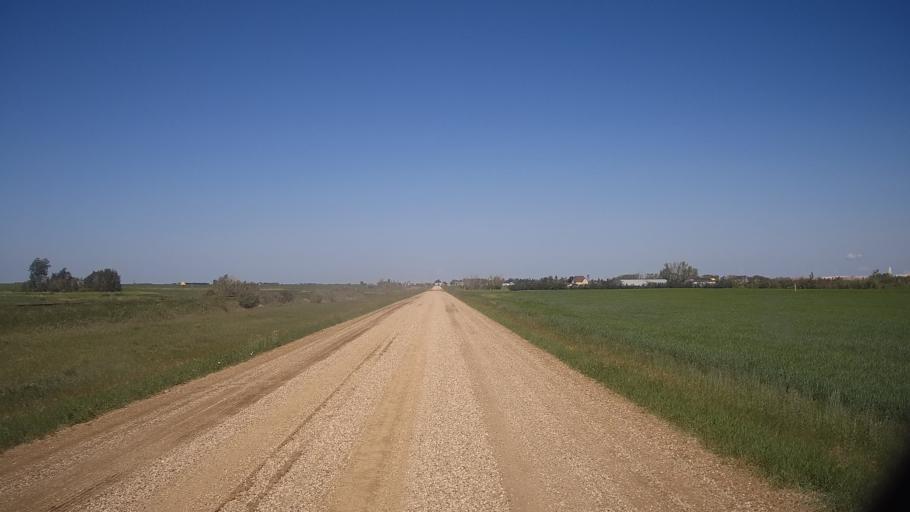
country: CA
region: Saskatchewan
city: Watrous
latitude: 51.8834
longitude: -106.0295
